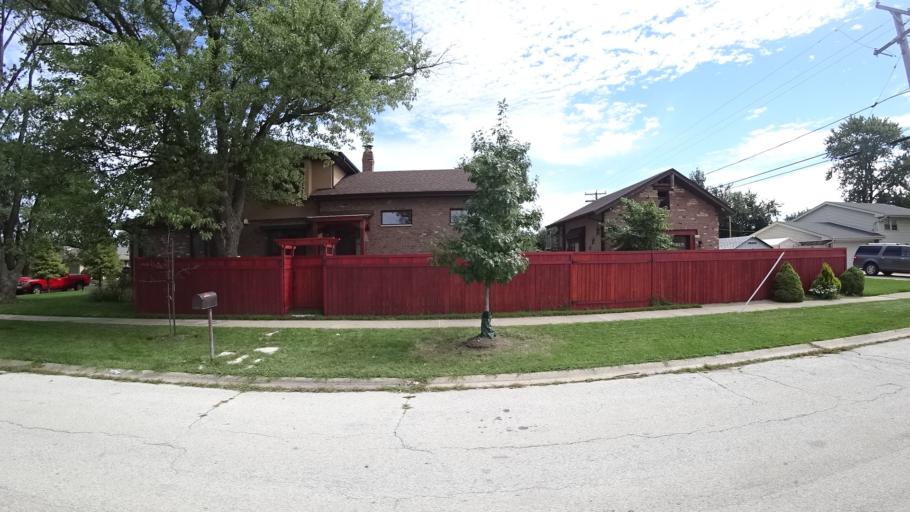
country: US
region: Illinois
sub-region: Cook County
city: Burbank
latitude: 41.7220
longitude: -87.7776
